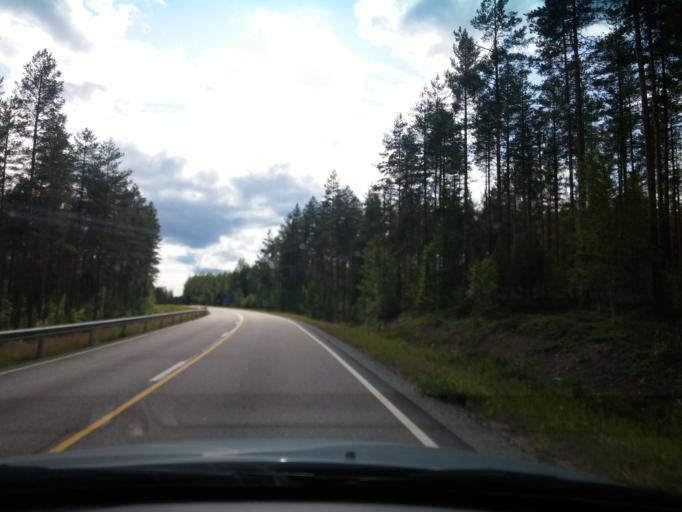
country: FI
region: Central Finland
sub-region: Saarijaervi-Viitasaari
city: Pylkoenmaeki
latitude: 62.5927
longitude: 24.6001
